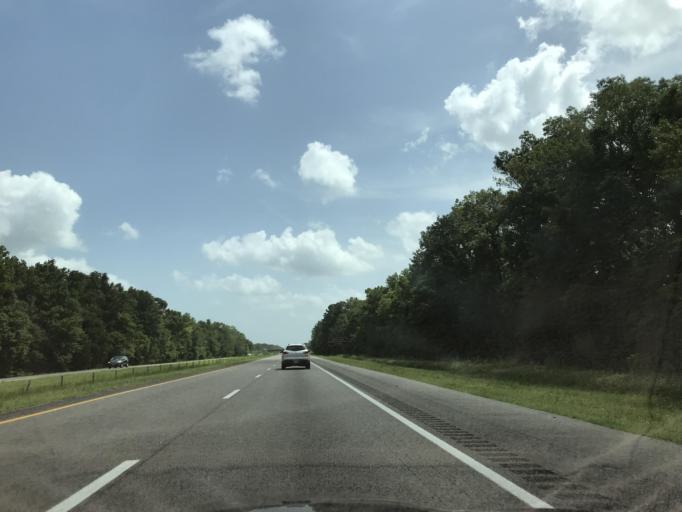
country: US
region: North Carolina
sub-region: Pender County
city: Rocky Point
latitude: 34.4500
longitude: -77.8770
